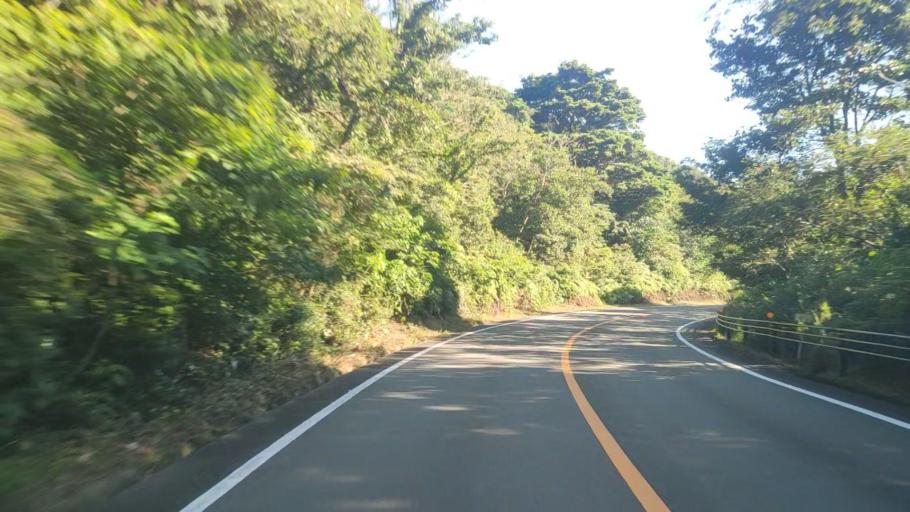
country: JP
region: Mie
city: Toba
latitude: 34.4066
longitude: 136.8904
